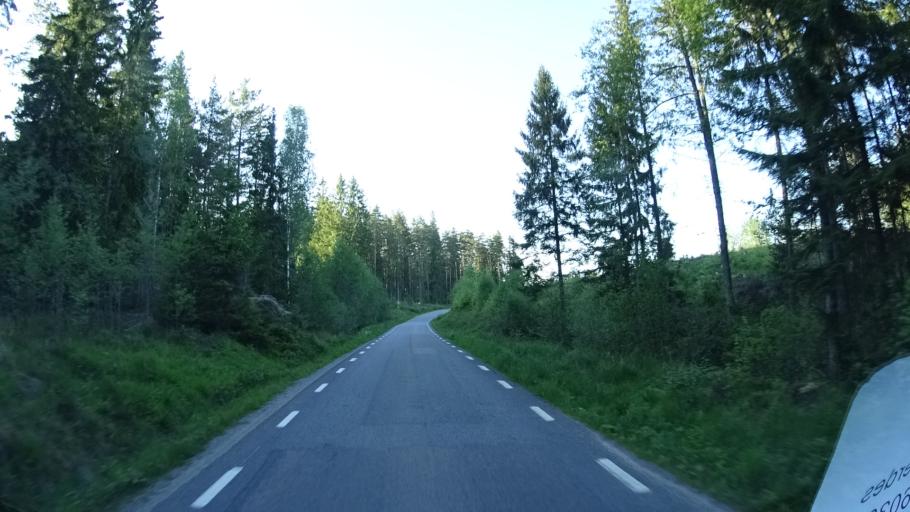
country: SE
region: OEstergoetland
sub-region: Finspangs Kommun
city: Finspang
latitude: 58.6496
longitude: 15.6775
